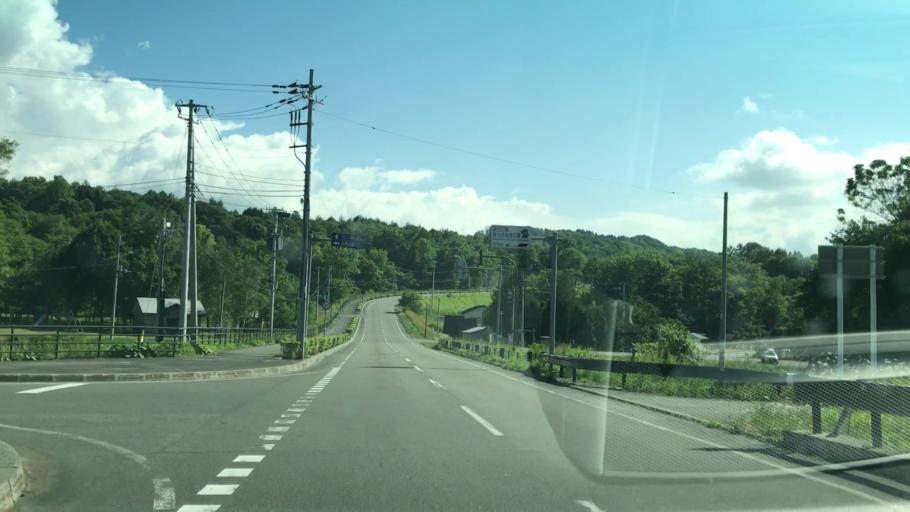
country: JP
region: Hokkaido
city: Shimo-furano
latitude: 42.8711
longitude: 142.4427
